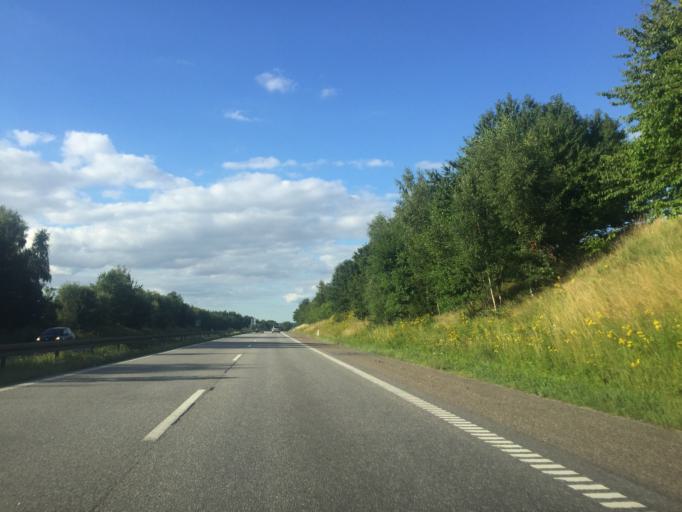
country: DK
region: Zealand
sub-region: Faxe Kommune
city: Ronnede
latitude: 55.2439
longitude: 11.9860
